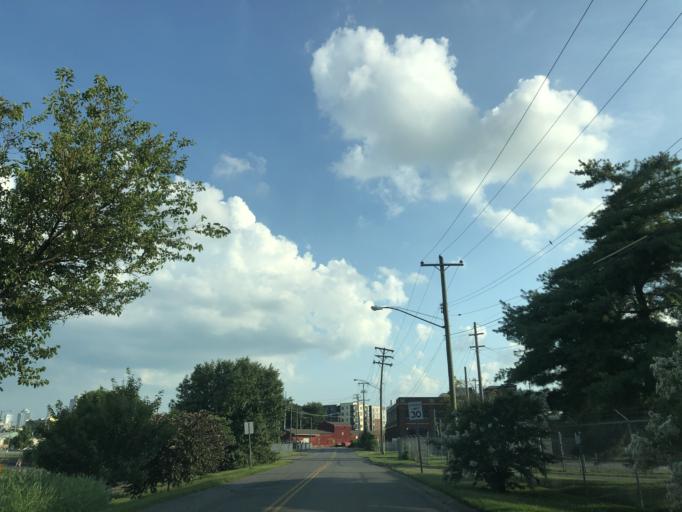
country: US
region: Tennessee
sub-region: Davidson County
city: Nashville
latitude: 36.1837
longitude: -86.7869
